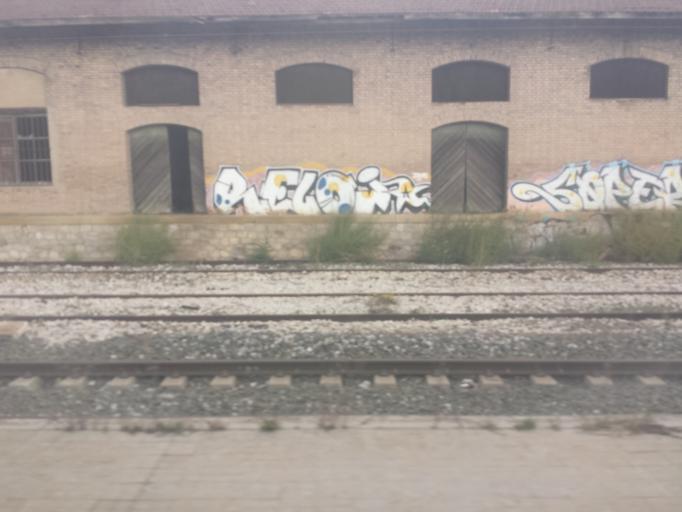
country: ES
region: Aragon
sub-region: Provincia de Zaragoza
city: Sobradiel
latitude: 41.7228
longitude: -1.0196
